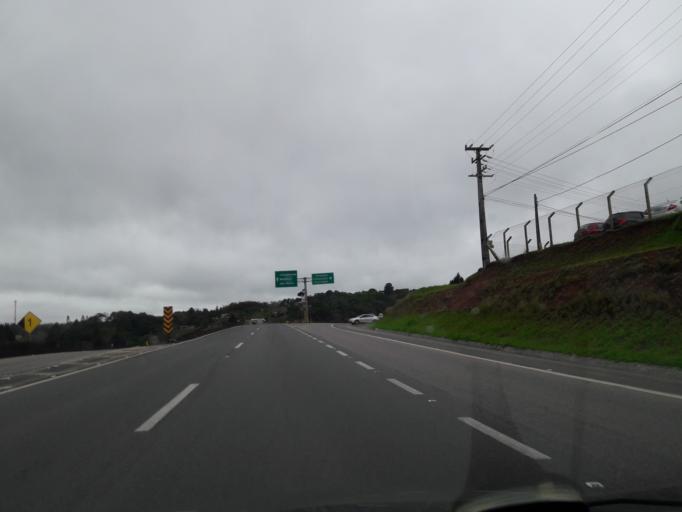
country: BR
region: Parana
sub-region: Quatro Barras
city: Quatro Barras
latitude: -25.3471
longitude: -49.0470
